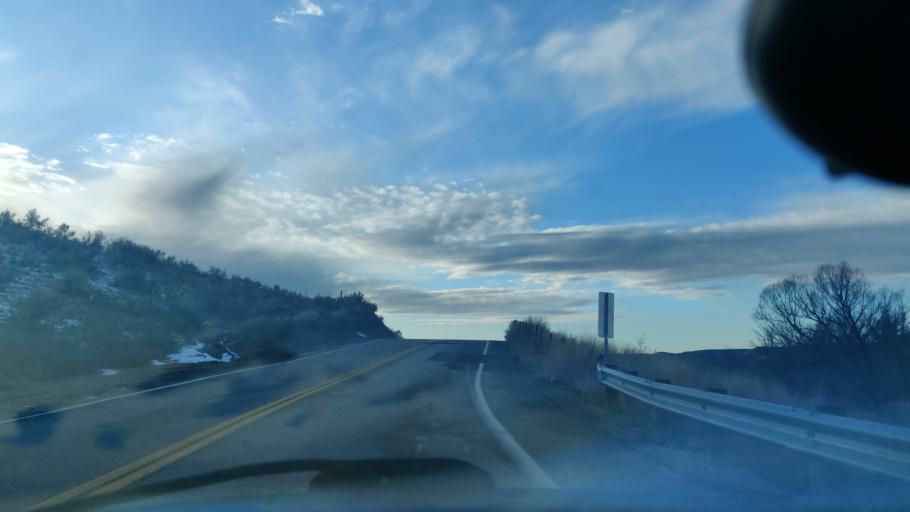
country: US
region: Idaho
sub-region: Ada County
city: Eagle
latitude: 43.7303
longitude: -116.2865
